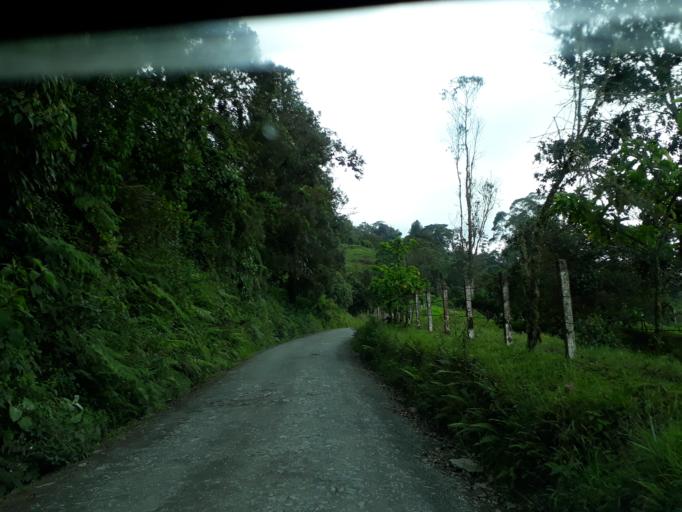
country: CO
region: Cundinamarca
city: Pacho
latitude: 5.2545
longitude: -74.1799
